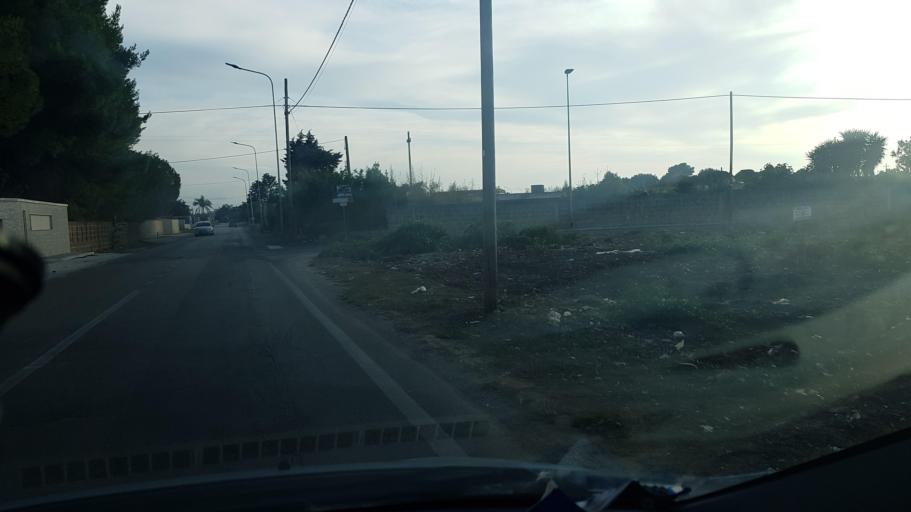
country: IT
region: Apulia
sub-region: Provincia di Lecce
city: Carmiano
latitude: 40.3365
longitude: 18.0409
